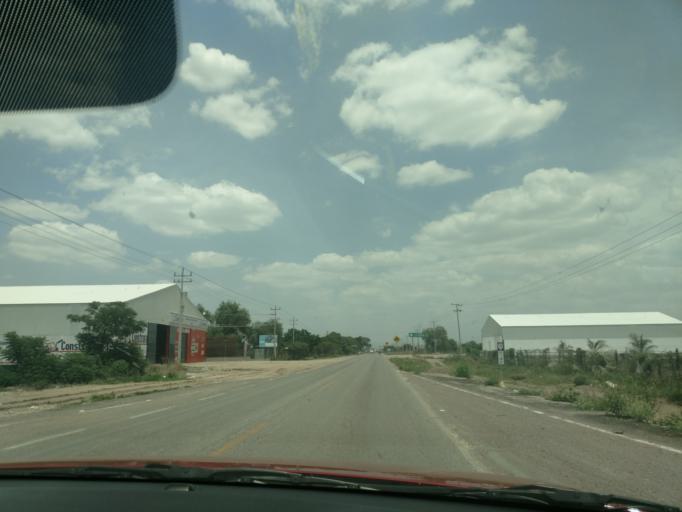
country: MX
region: San Luis Potosi
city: Ciudad Fernandez
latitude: 21.9449
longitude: -100.0496
